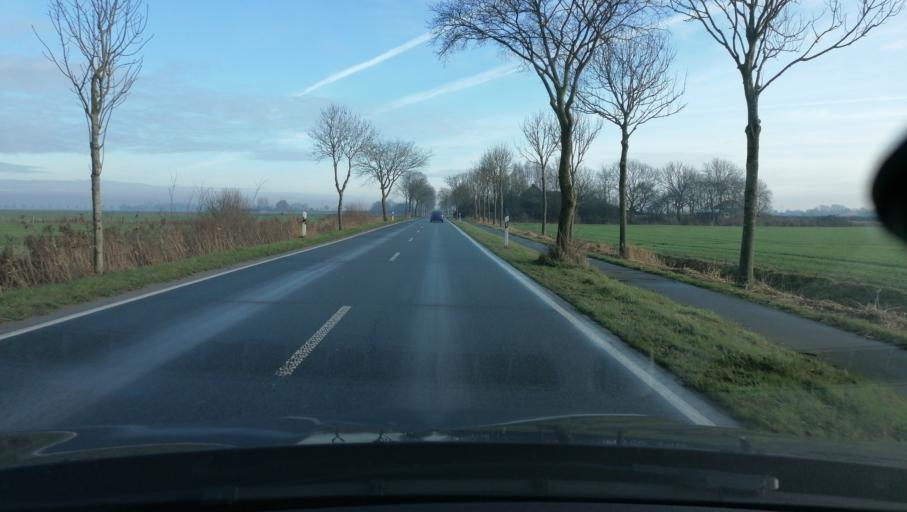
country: DE
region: Schleswig-Holstein
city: Wohrden
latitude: 54.1215
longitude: 8.9967
